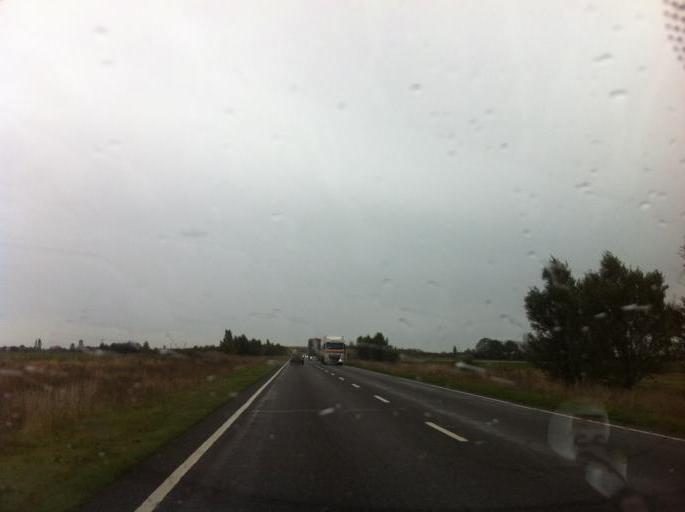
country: GB
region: England
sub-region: Lincolnshire
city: Crowland
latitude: 52.6550
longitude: -0.1866
